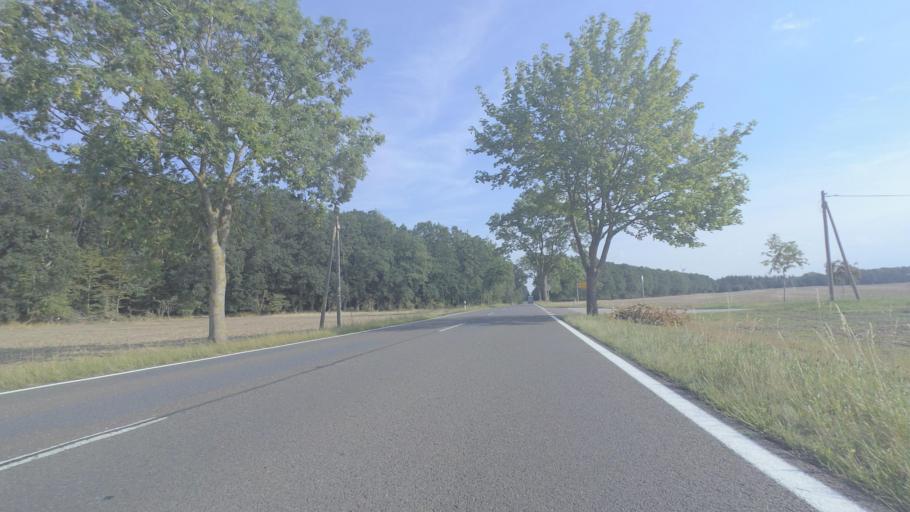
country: DE
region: Mecklenburg-Vorpommern
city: Grimmen
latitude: 54.0323
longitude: 13.1299
